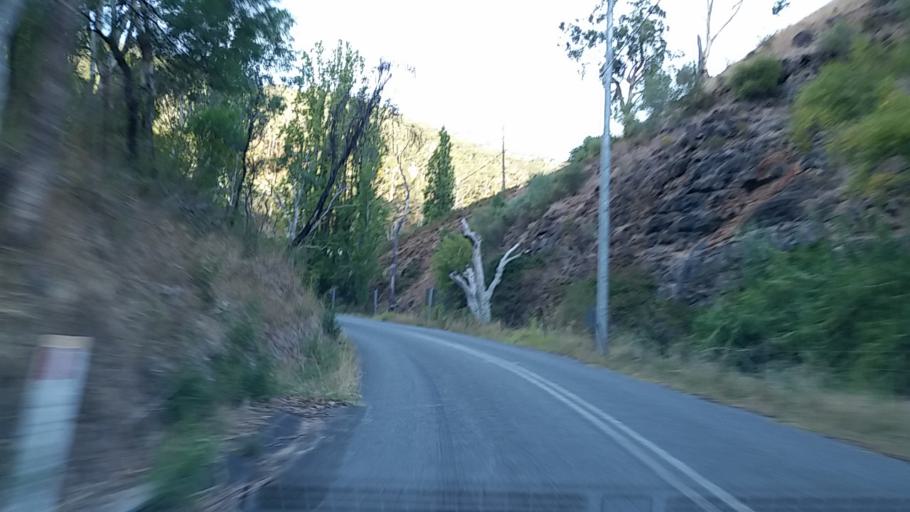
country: AU
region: South Australia
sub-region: Campbelltown
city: Athelstone
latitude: -34.8712
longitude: 138.7527
